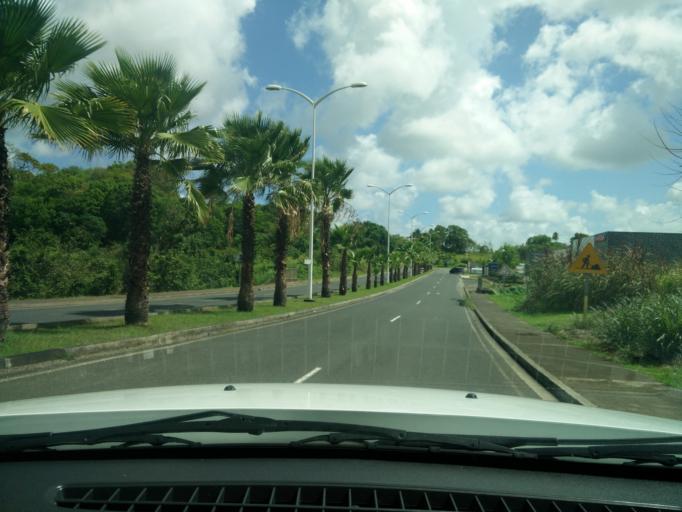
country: GP
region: Guadeloupe
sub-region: Guadeloupe
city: Les Abymes
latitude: 16.2701
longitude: -61.5176
